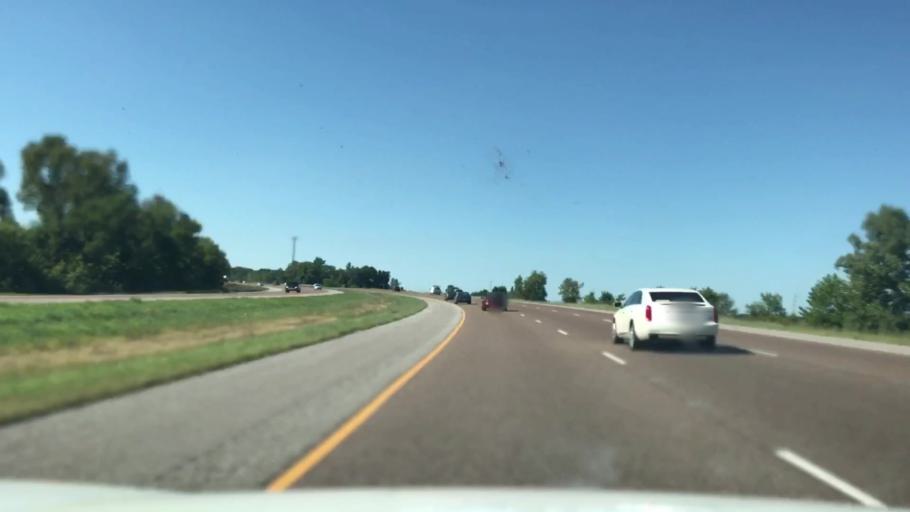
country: US
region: Illinois
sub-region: Madison County
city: Glen Carbon
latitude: 38.7181
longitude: -90.0256
